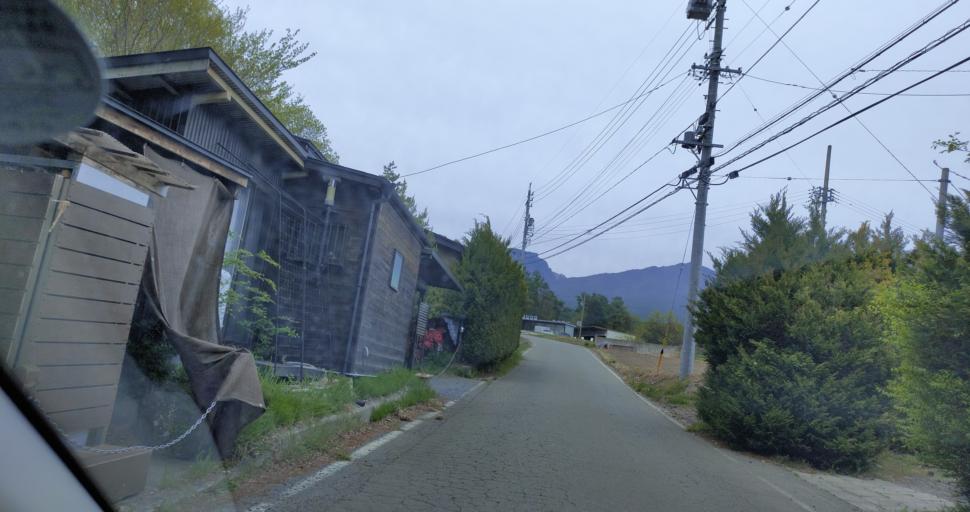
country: JP
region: Nagano
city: Komoro
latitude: 36.3376
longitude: 138.4675
